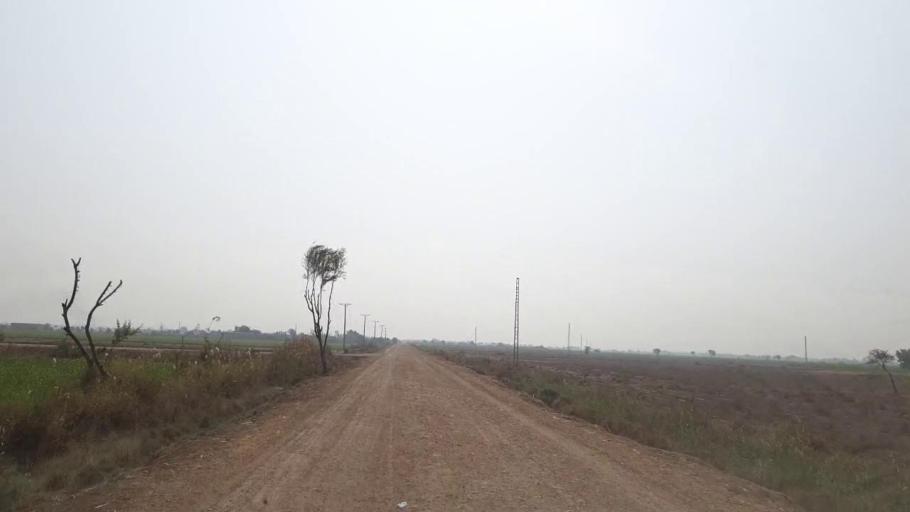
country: PK
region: Sindh
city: Mirpur Khas
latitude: 25.5471
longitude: 69.0592
